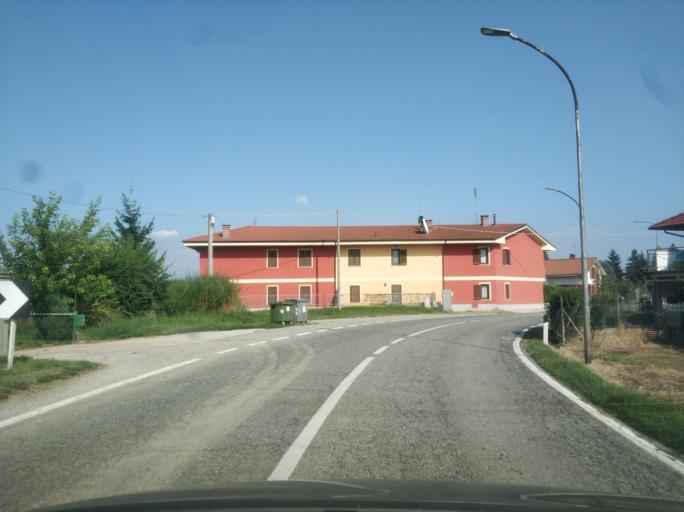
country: IT
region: Piedmont
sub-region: Provincia di Cuneo
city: Centallo
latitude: 44.5035
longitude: 7.5795
